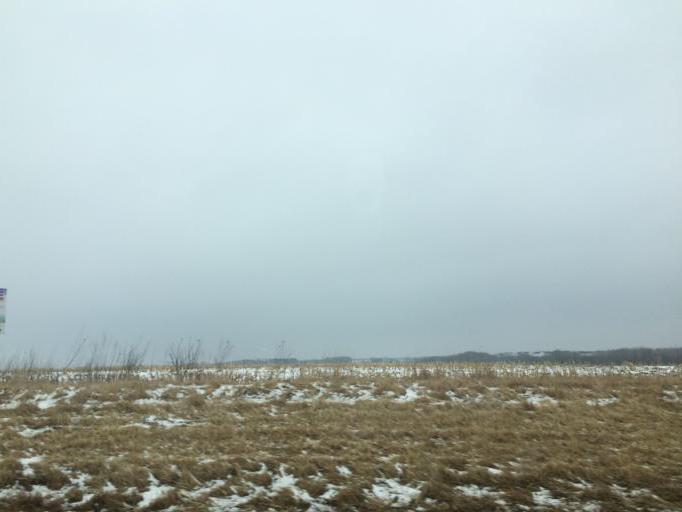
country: US
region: Illinois
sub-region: McHenry County
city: Huntley
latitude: 42.2060
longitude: -88.4225
